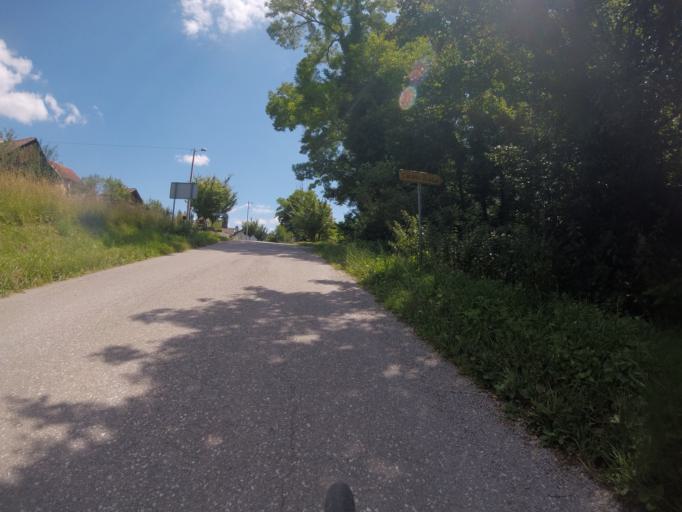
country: HR
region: Karlovacka
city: Ozalj
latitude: 45.6697
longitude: 15.4745
